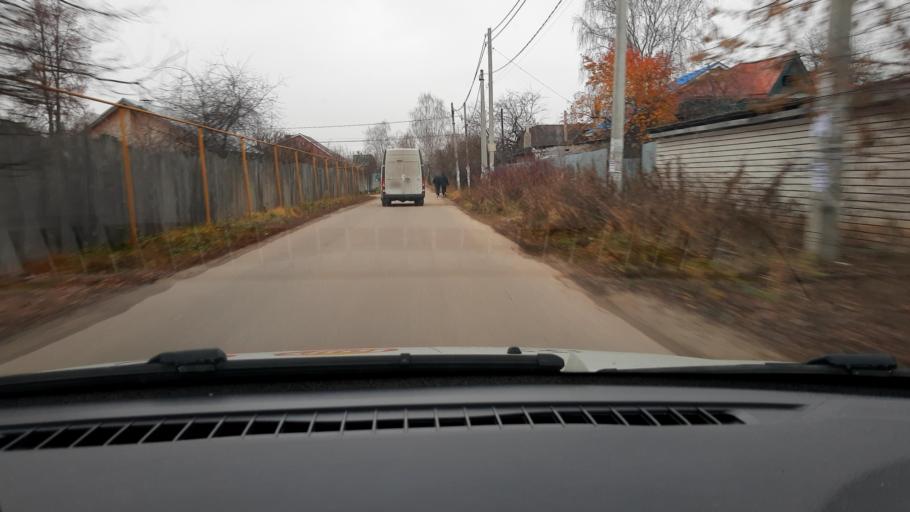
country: RU
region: Nizjnij Novgorod
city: Burevestnik
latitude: 56.2007
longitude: 43.7735
